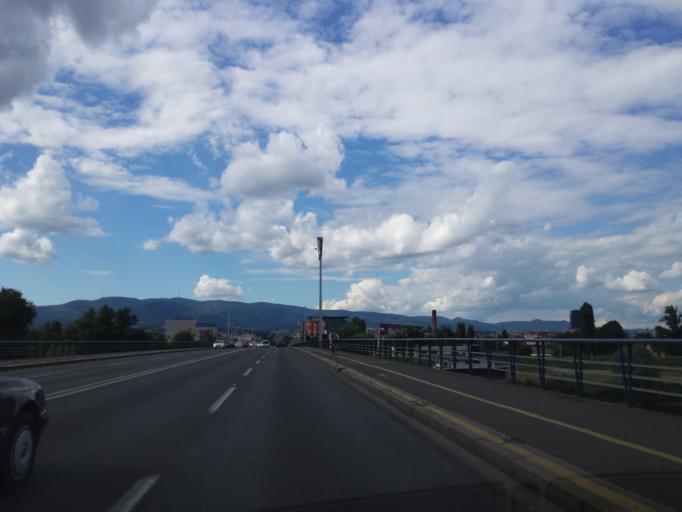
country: HR
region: Grad Zagreb
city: Novi Zagreb
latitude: 45.7887
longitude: 15.9797
